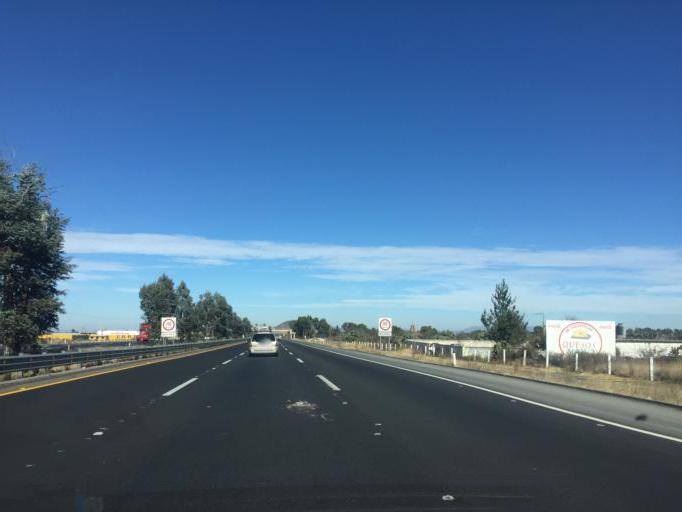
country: MX
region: Mexico
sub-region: Aculco
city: El Colorado
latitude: 20.1782
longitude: -99.7633
